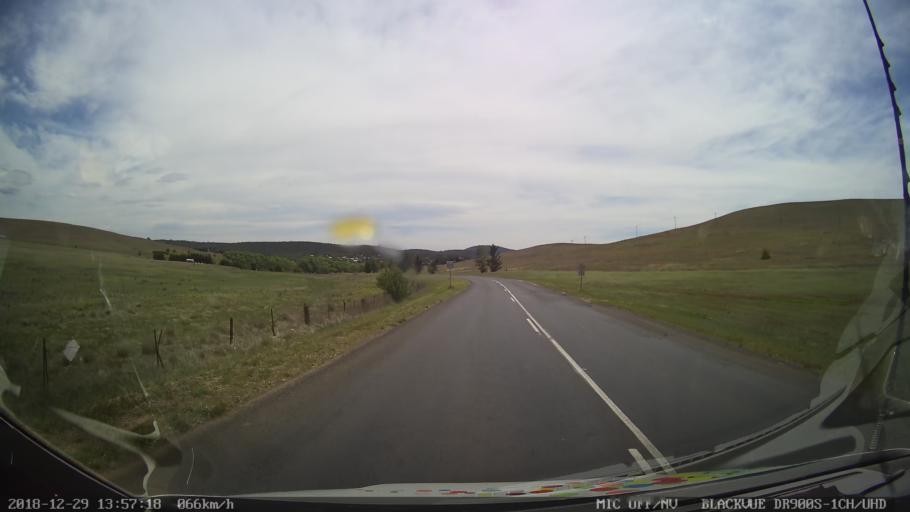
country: AU
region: New South Wales
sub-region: Cooma-Monaro
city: Cooma
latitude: -36.2393
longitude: 149.1436
